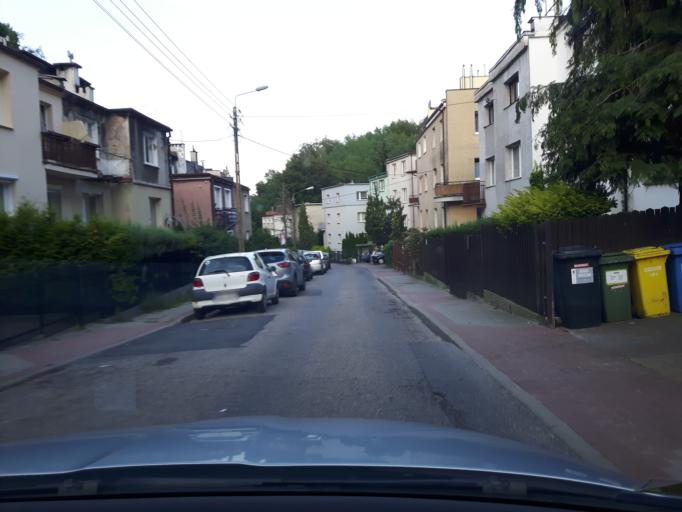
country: PL
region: Pomeranian Voivodeship
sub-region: Gdynia
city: Gdynia
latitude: 54.5129
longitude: 18.5257
